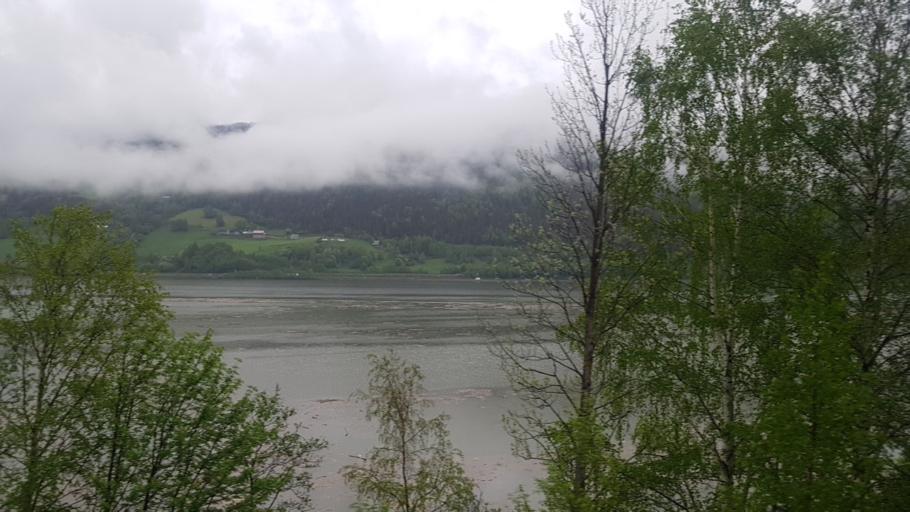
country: NO
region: Oppland
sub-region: Oyer
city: Tretten
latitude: 61.3973
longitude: 10.2353
